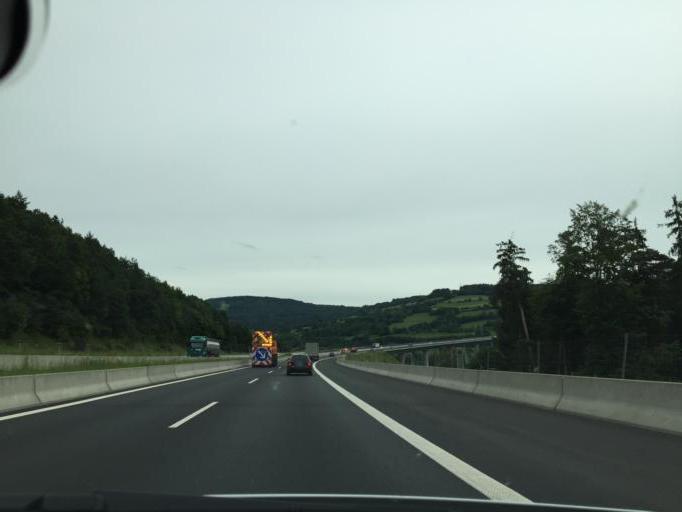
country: DE
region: Bavaria
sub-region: Regierungsbezirk Unterfranken
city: Riedenberg
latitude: 50.3201
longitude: 9.8342
